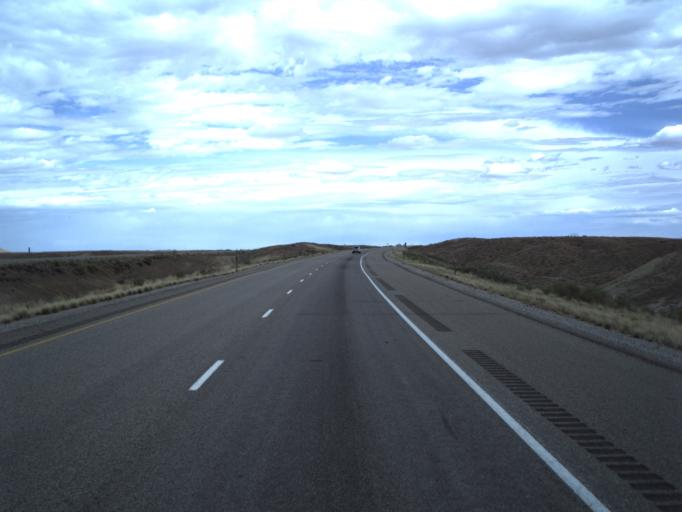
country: US
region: Utah
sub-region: Grand County
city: Moab
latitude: 38.9254
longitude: -109.9851
